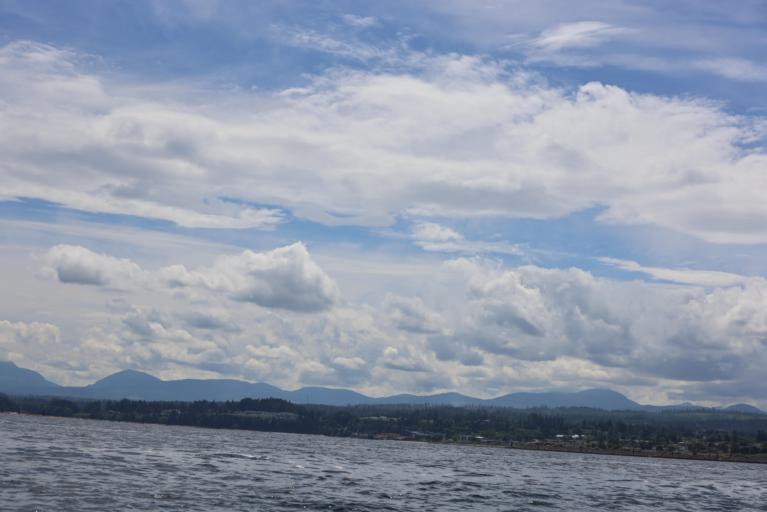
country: CA
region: British Columbia
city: Nanaimo
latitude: 49.1662
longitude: -123.9157
